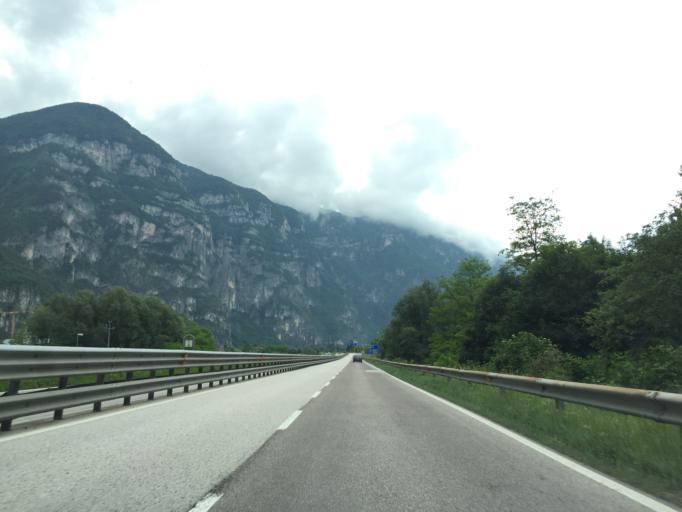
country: IT
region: Trentino-Alto Adige
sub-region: Provincia di Trento
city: Grigno
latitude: 46.0139
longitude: 11.6227
